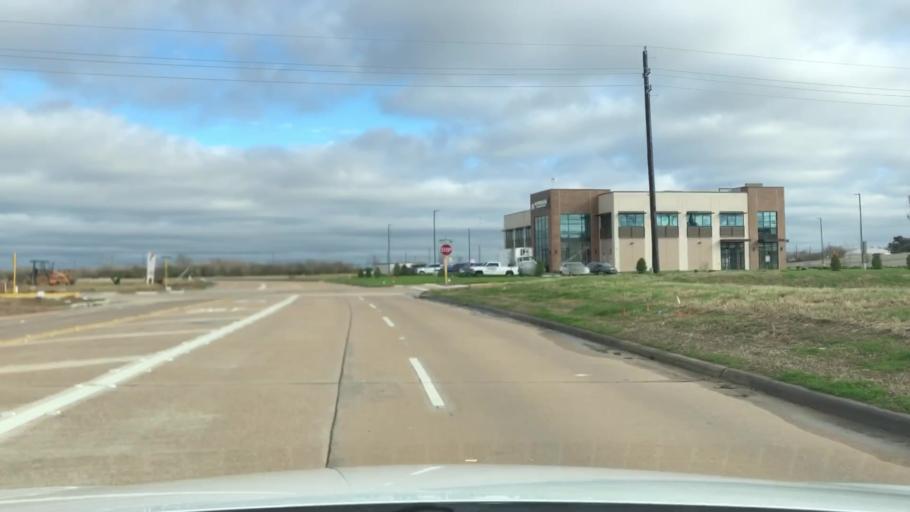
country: US
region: Texas
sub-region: Fort Bend County
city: Cinco Ranch
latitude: 29.7873
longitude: -95.7714
